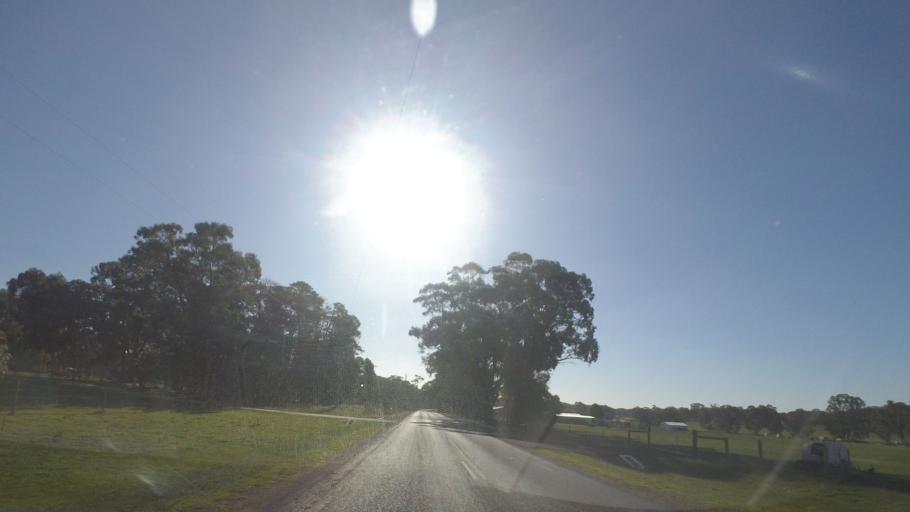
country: AU
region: Victoria
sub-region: Greater Bendigo
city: Kangaroo Flat
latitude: -36.8559
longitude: 144.2815
